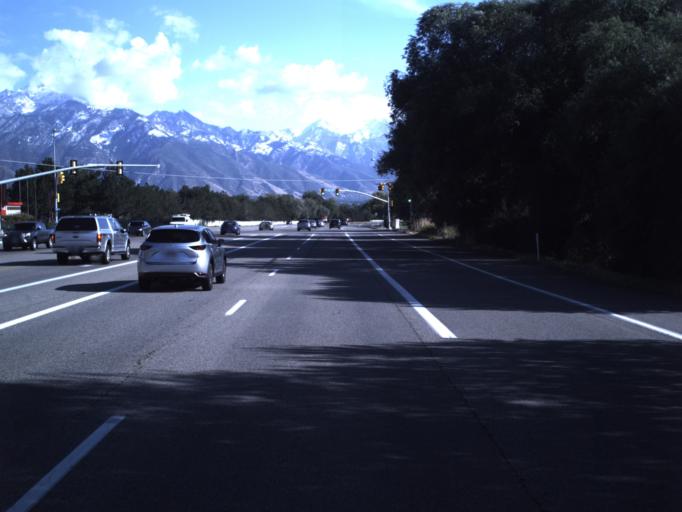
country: US
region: Utah
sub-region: Salt Lake County
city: Holladay
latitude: 40.6598
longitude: -111.8554
